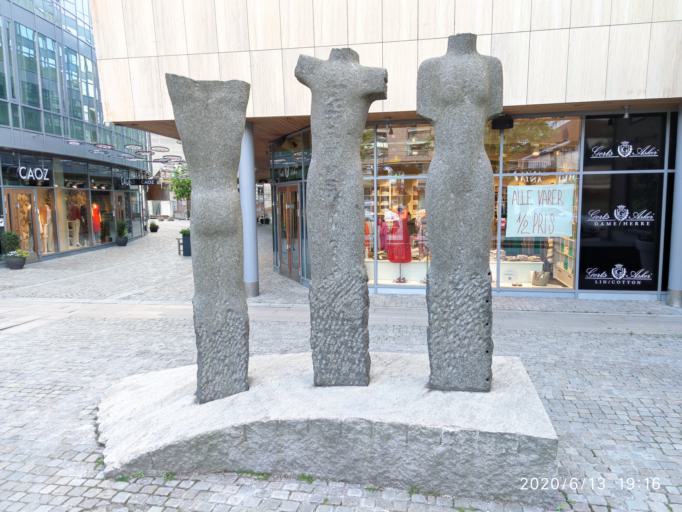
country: NO
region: Akershus
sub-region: Asker
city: Asker
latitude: 59.8354
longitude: 10.4336
